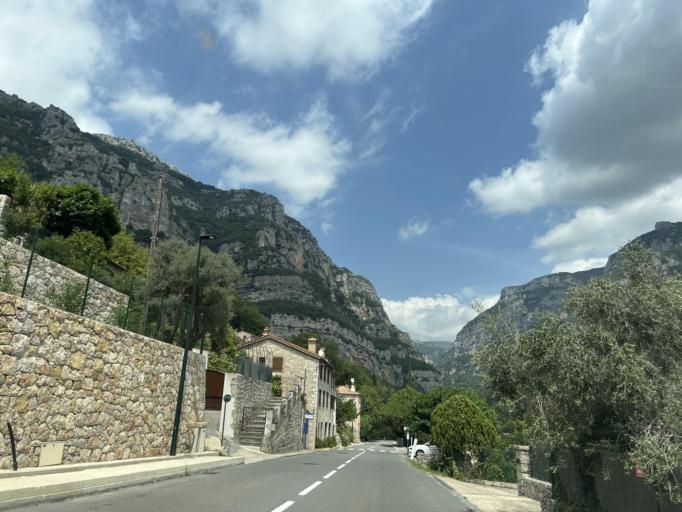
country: FR
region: Provence-Alpes-Cote d'Azur
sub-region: Departement des Alpes-Maritimes
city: Le Rouret
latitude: 43.7160
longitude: 6.9894
